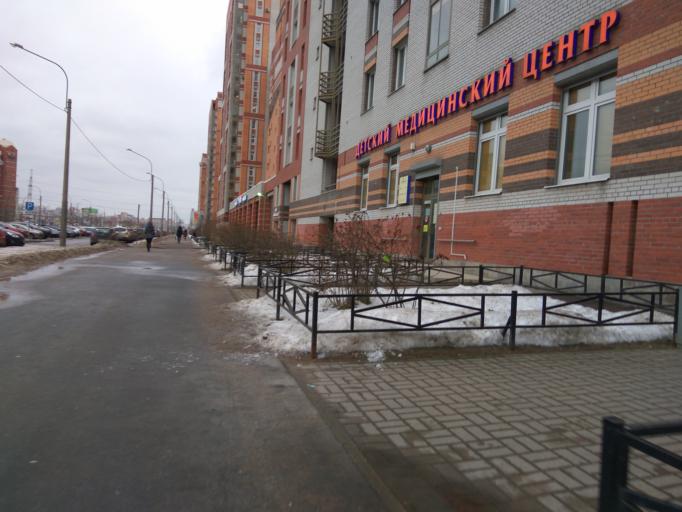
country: RU
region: St.-Petersburg
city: Staraya Derevnya
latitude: 60.0018
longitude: 30.2468
